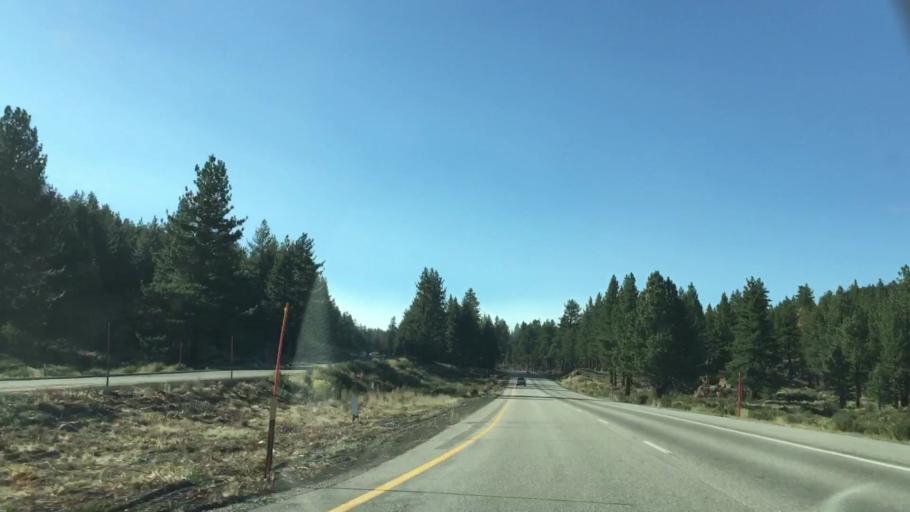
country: US
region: California
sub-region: Mono County
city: Mammoth Lakes
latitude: 37.6579
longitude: -118.9258
